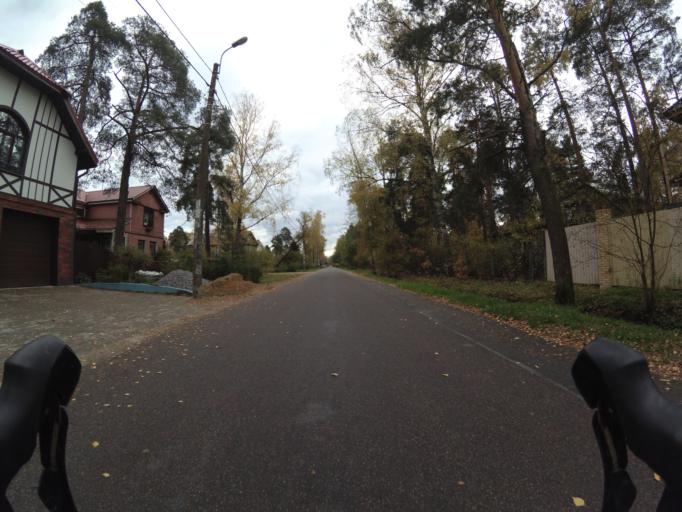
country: RU
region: St.-Petersburg
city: Lakhtinskiy
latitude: 60.0011
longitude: 30.1314
